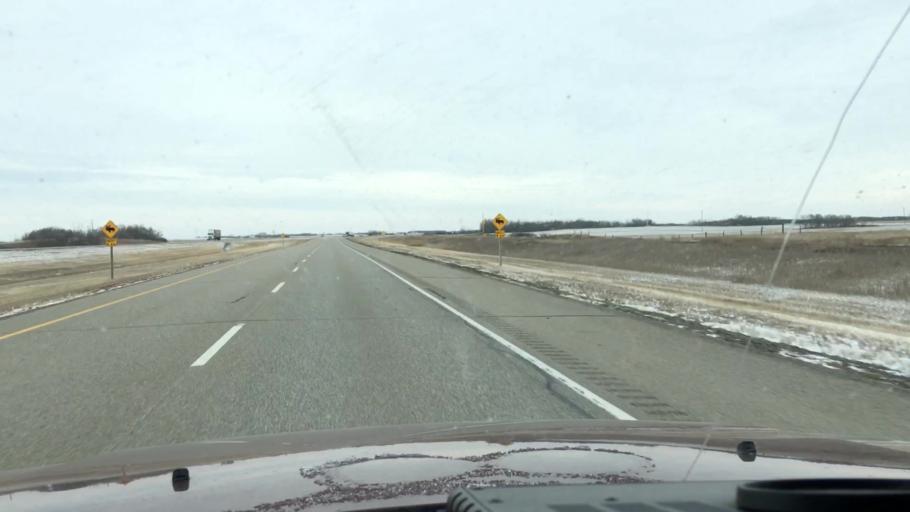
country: CA
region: Saskatchewan
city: Watrous
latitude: 51.3373
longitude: -106.0912
